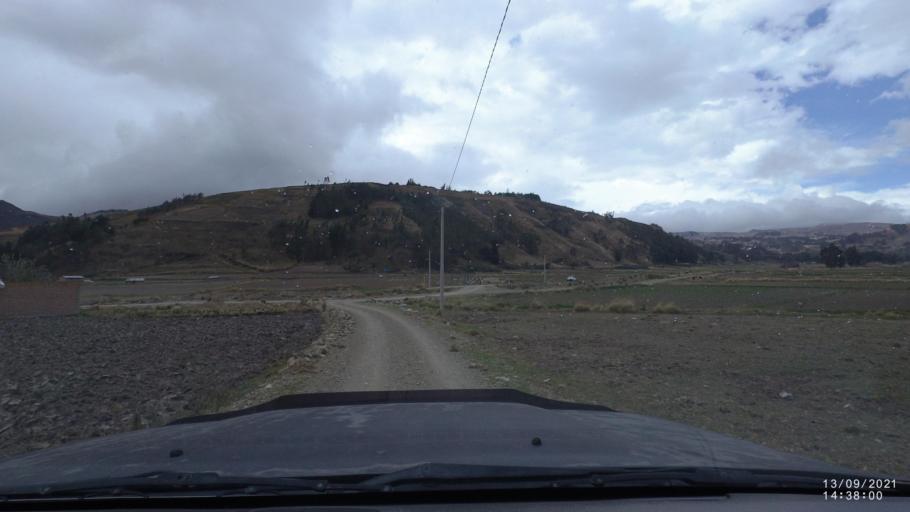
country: BO
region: Cochabamba
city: Colomi
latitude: -17.3707
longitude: -65.8334
